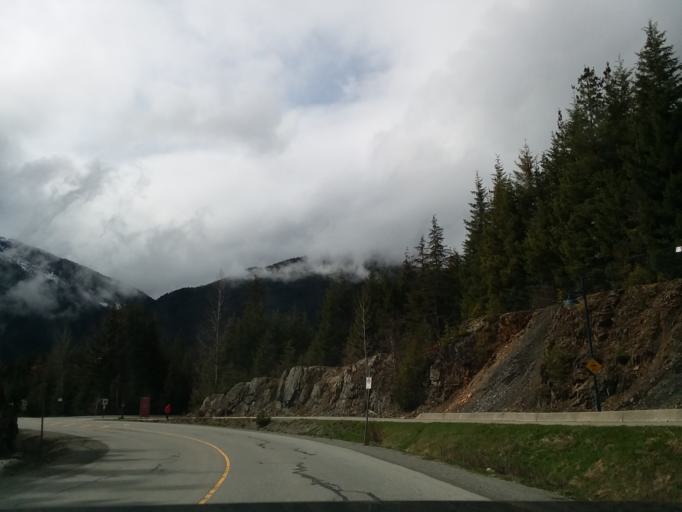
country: CA
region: British Columbia
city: Whistler
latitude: 50.1272
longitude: -122.9630
